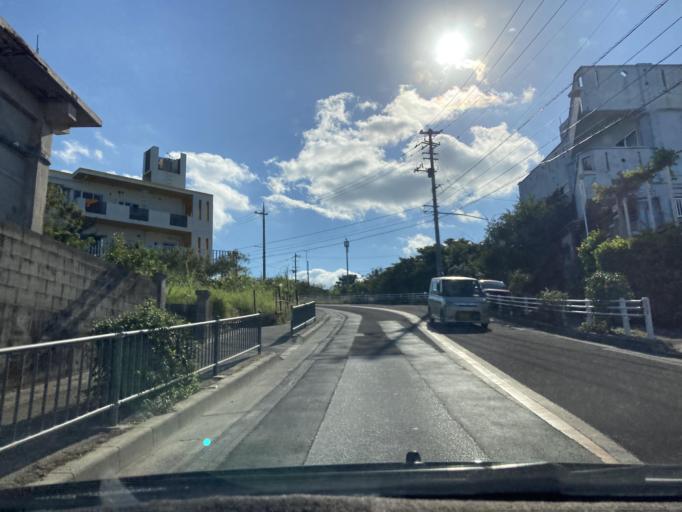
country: JP
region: Okinawa
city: Katsuren-haebaru
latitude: 26.3200
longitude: 127.9095
